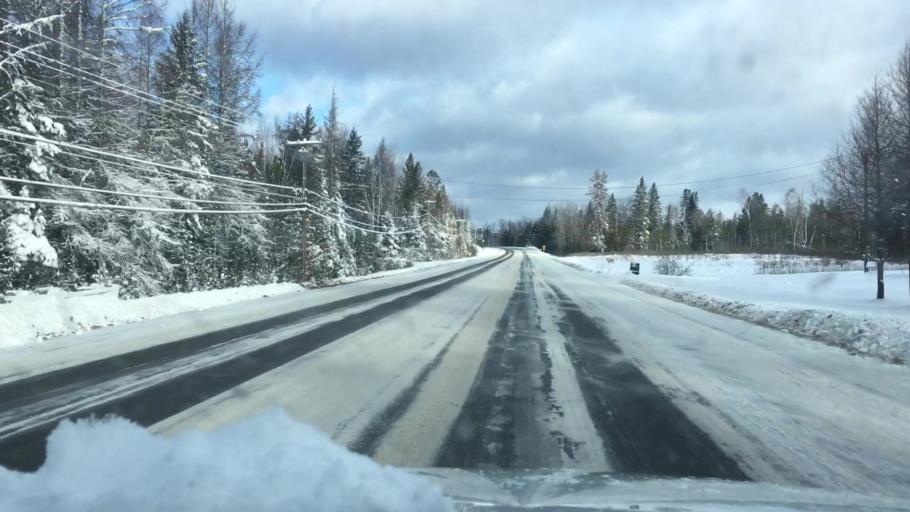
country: US
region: Maine
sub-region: Aroostook County
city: Caribou
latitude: 46.9216
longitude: -68.0196
